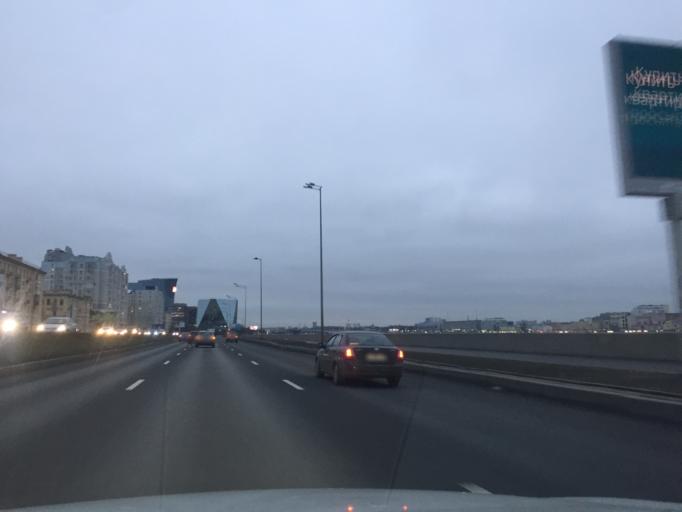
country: RU
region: St.-Petersburg
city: Centralniy
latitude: 59.9406
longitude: 30.4039
